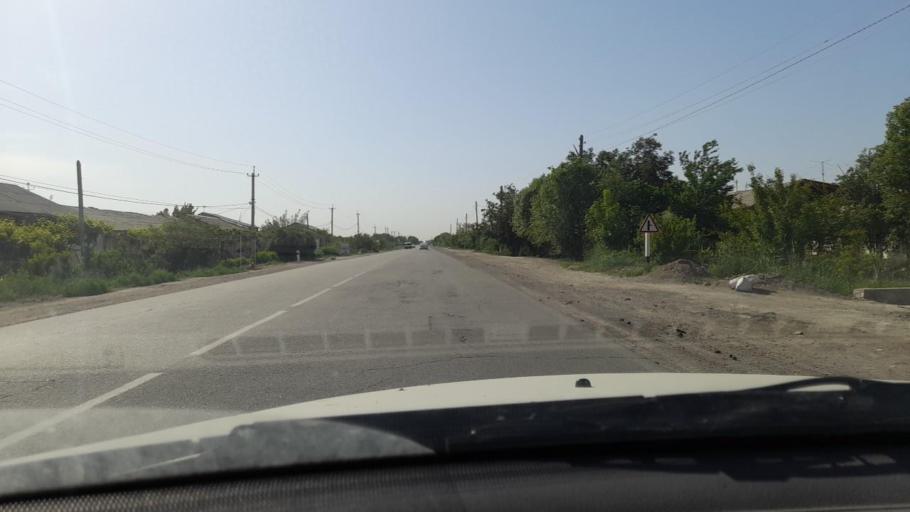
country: UZ
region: Bukhara
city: Romiton
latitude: 39.9017
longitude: 64.4055
